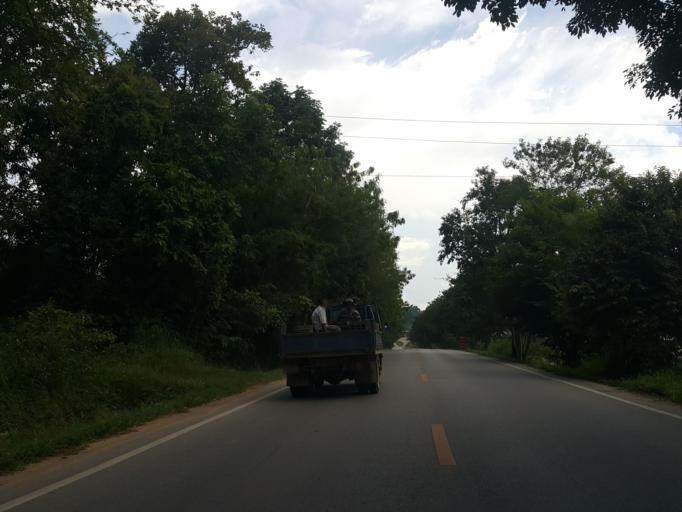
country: TH
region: Chiang Mai
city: Phrao
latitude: 19.2878
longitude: 99.1878
